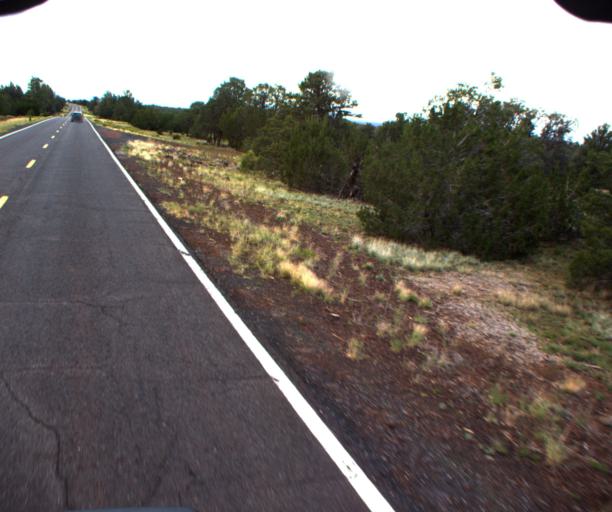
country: US
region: Arizona
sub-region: Coconino County
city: Parks
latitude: 35.5198
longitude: -111.8378
